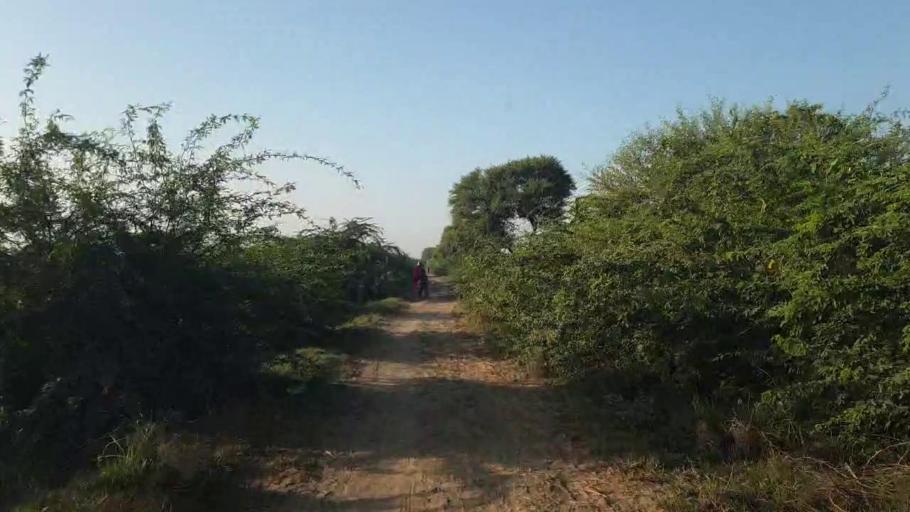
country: PK
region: Sindh
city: Badin
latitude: 24.6113
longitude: 68.7840
